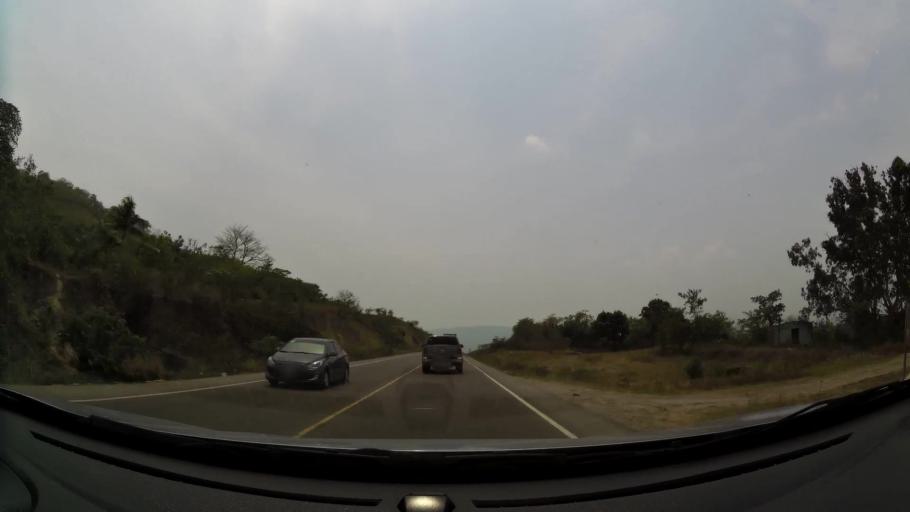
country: HN
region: Cortes
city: El Plan
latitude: 15.2641
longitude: -87.9641
